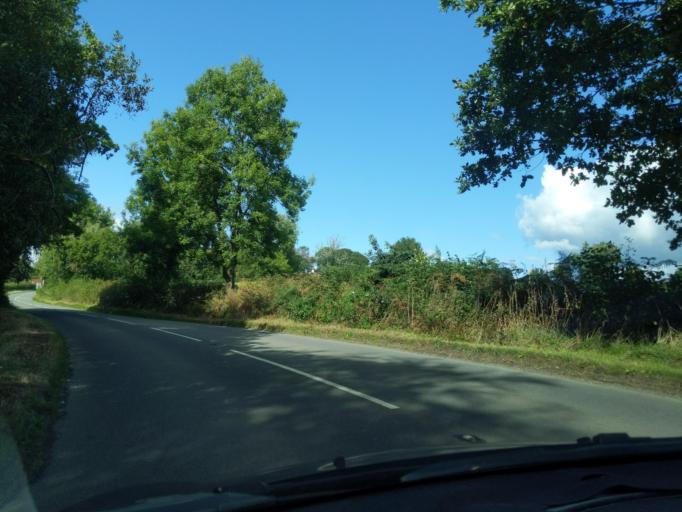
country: GB
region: England
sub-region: Cornwall
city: Werrington
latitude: 50.6971
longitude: -4.3217
